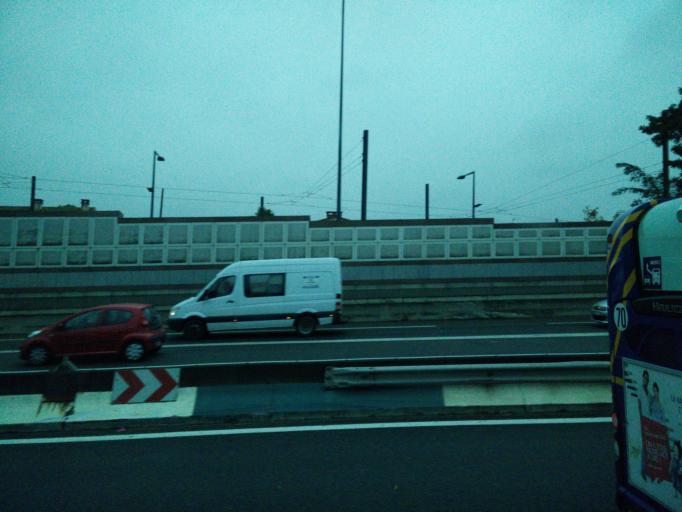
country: FR
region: Midi-Pyrenees
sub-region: Departement de la Haute-Garonne
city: Blagnac
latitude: 43.6218
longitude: 1.3925
